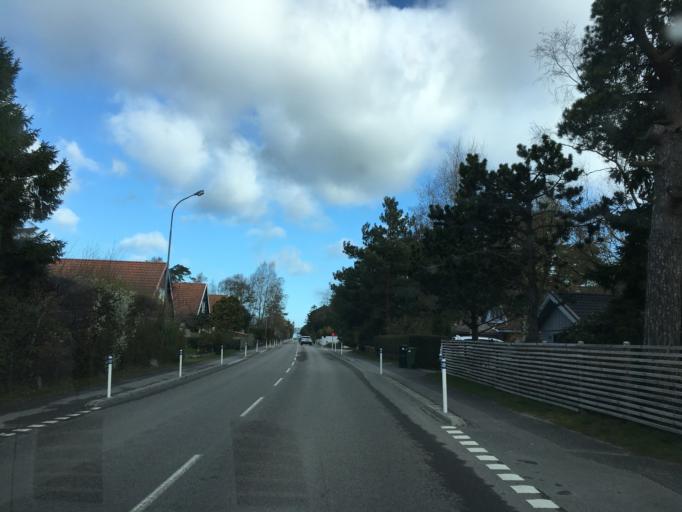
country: SE
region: Skane
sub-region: Vellinge Kommun
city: Hollviken
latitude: 55.4124
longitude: 12.9558
